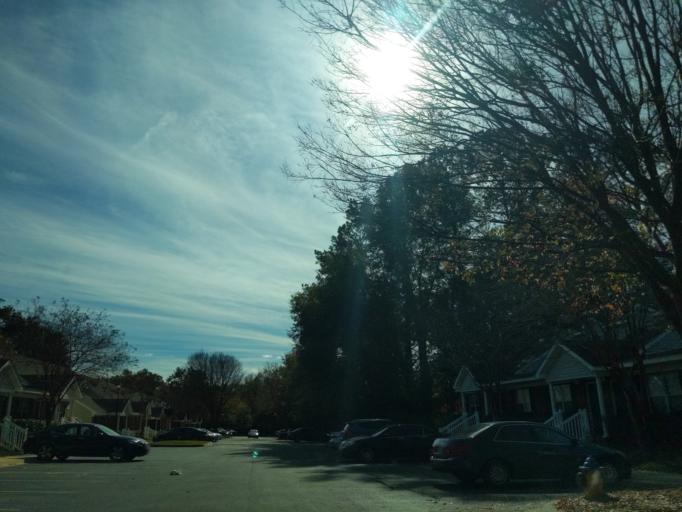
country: US
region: Florida
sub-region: Leon County
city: Tallahassee
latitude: 30.4671
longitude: -84.3411
